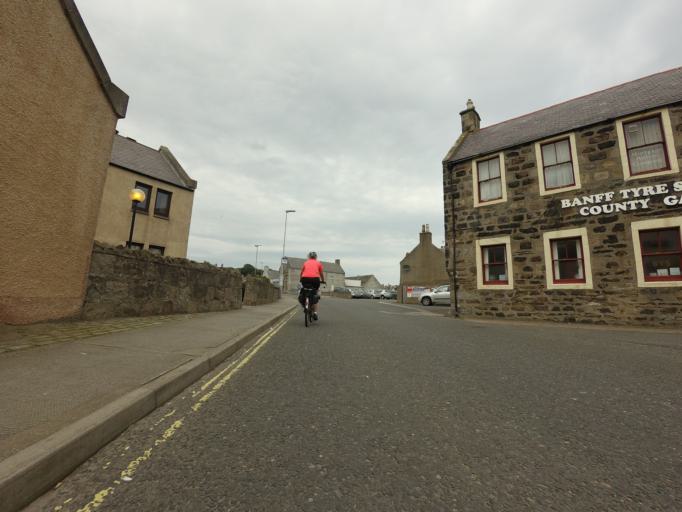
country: GB
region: Scotland
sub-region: Aberdeenshire
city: Banff
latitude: 57.6647
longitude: -2.5183
